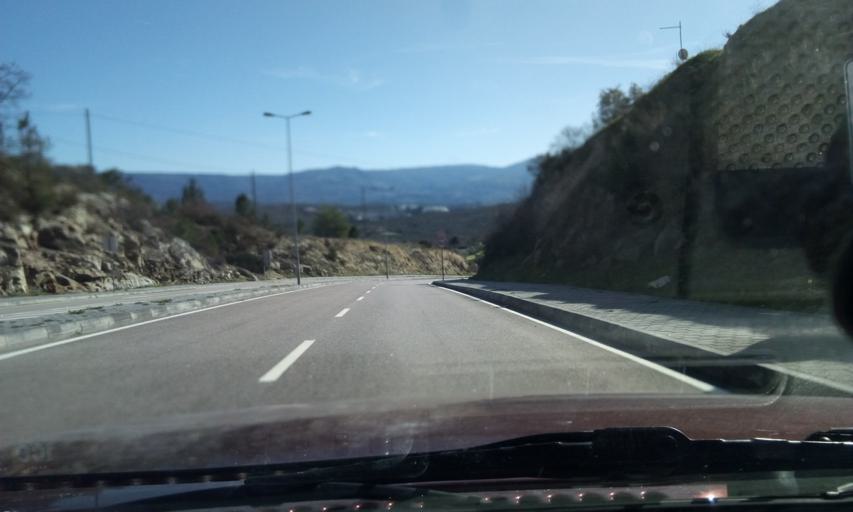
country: PT
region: Guarda
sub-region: Fornos de Algodres
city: Fornos de Algodres
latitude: 40.6145
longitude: -7.5381
